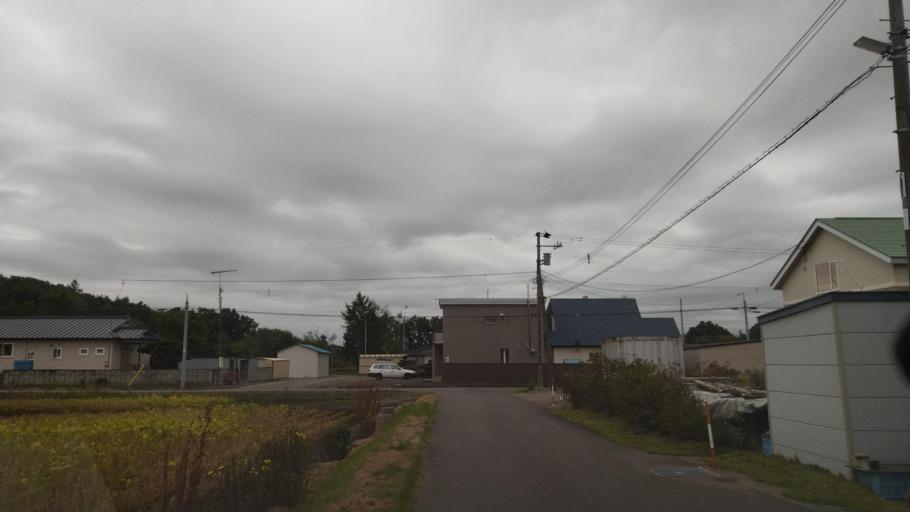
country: JP
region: Hokkaido
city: Otofuke
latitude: 43.2297
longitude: 143.2997
